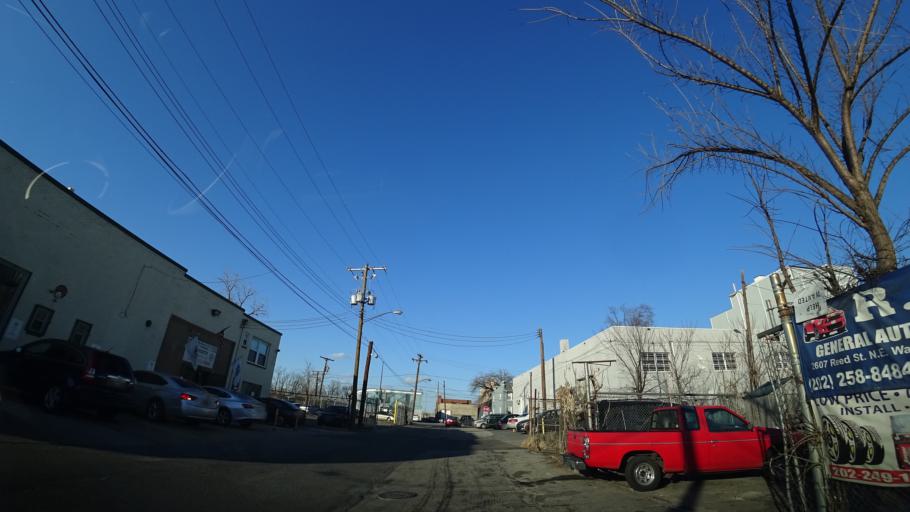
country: US
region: Maryland
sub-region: Prince George's County
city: Mount Rainier
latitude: 38.9239
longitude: -76.9939
